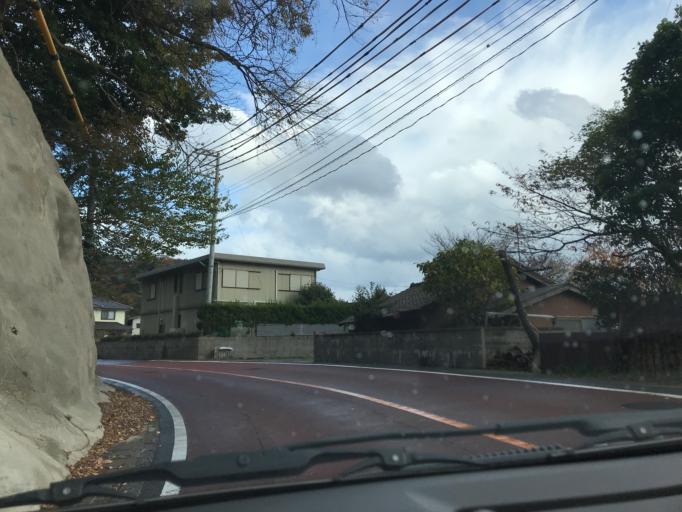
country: JP
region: Shimane
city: Sakaiminato
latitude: 35.5502
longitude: 133.2302
